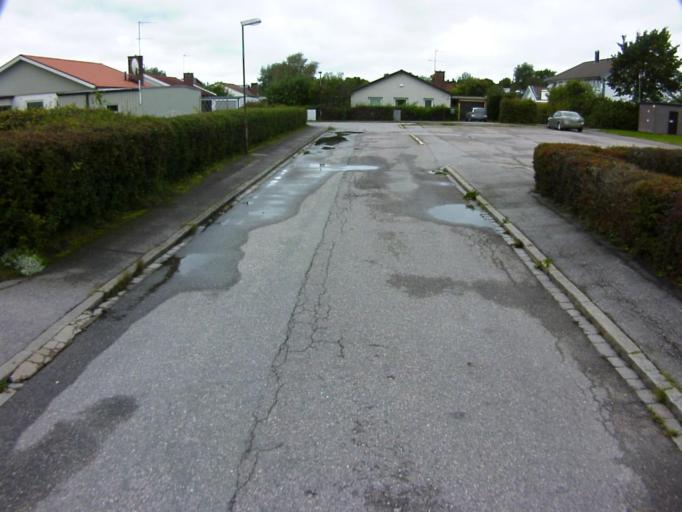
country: SE
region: Soedermanland
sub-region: Eskilstuna Kommun
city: Eskilstuna
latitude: 59.3772
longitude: 16.4801
